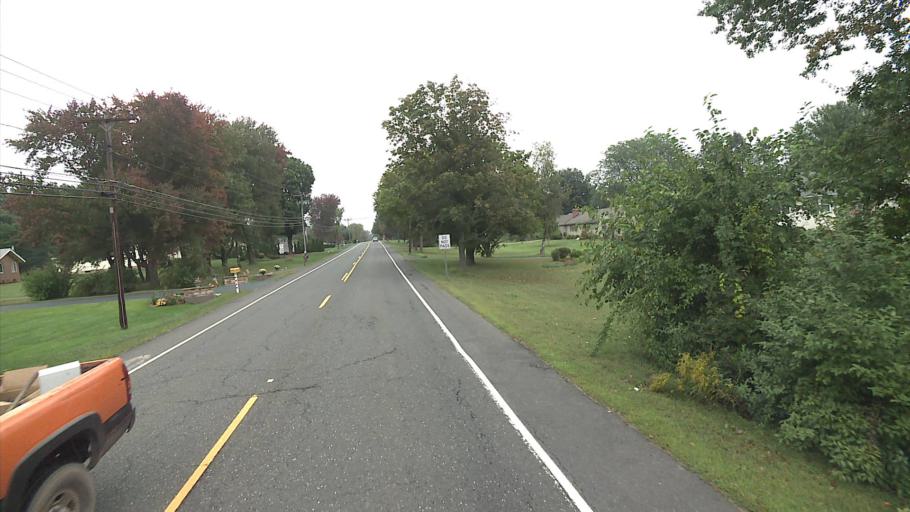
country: US
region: Connecticut
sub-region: Hartford County
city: Suffield Depot
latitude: 42.0137
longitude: -72.6411
